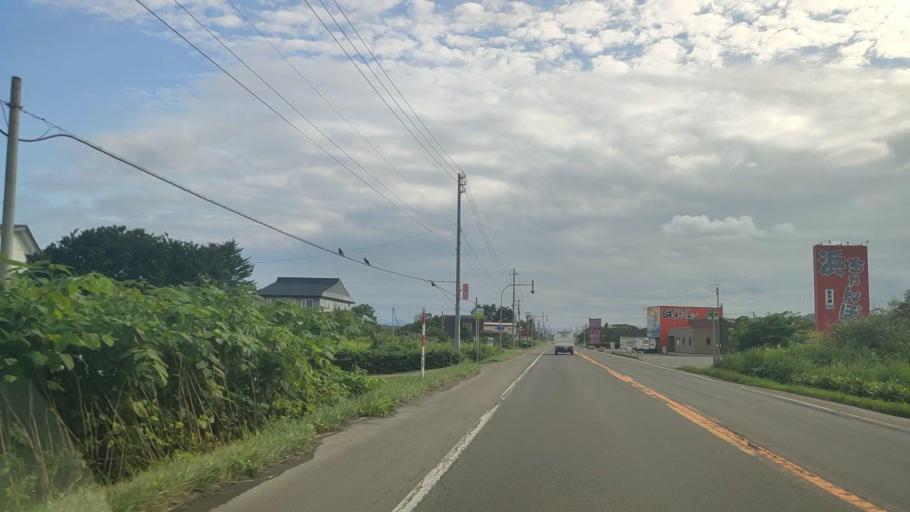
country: JP
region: Hokkaido
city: Niseko Town
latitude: 42.4801
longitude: 140.3500
